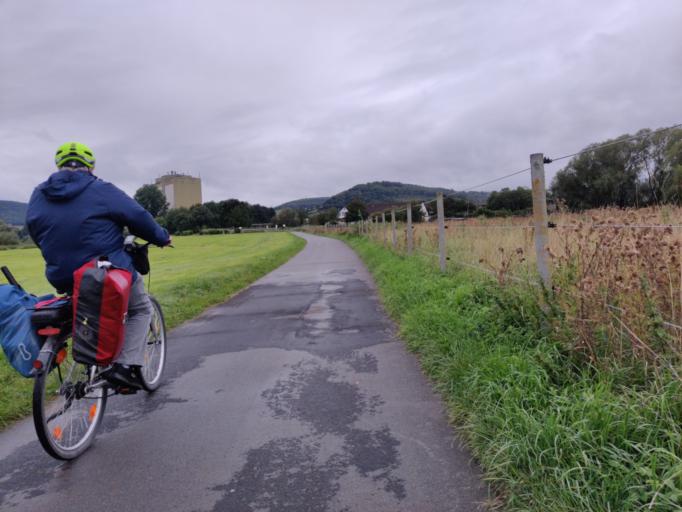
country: DE
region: North Rhine-Westphalia
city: Beverungen
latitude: 51.6717
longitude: 9.3865
